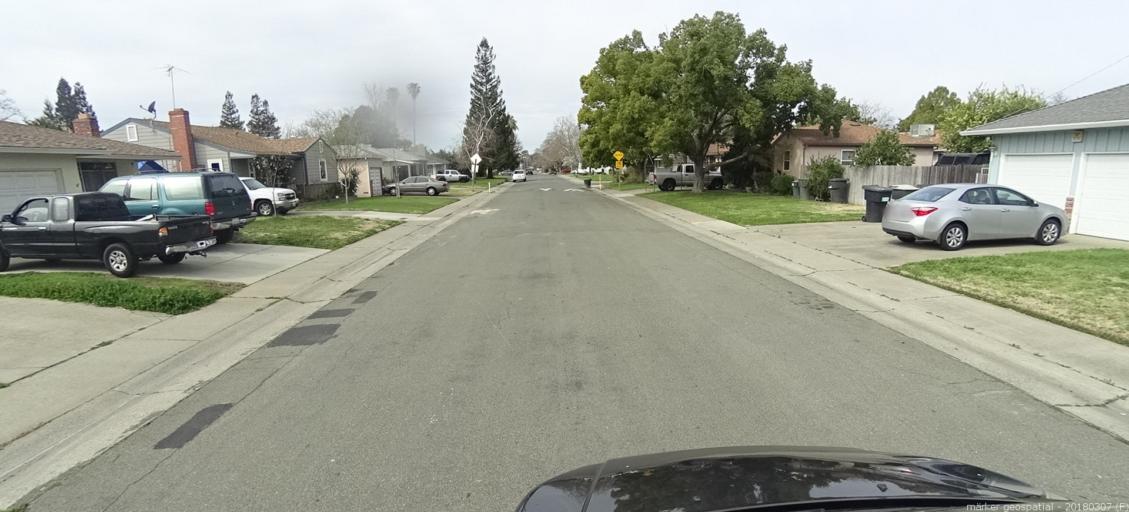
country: US
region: California
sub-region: Sacramento County
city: Parkway
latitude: 38.5272
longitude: -121.4537
